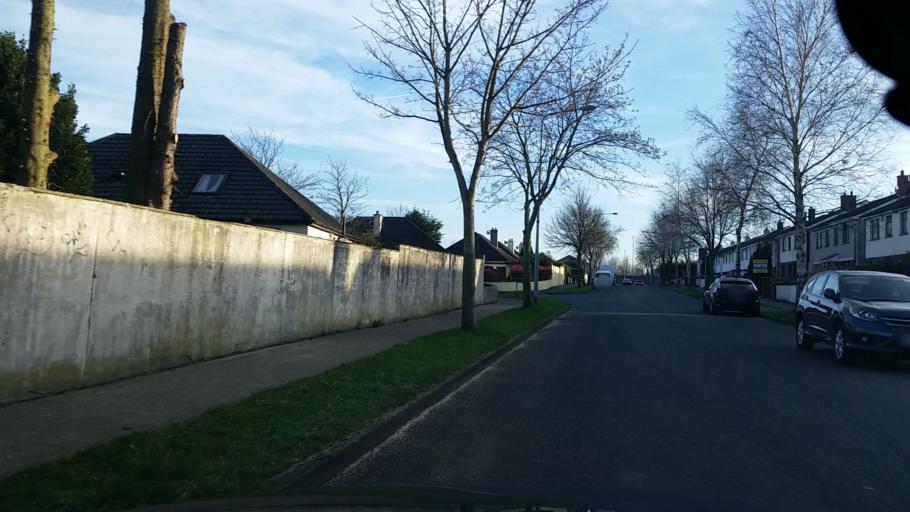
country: IE
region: Leinster
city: Hartstown
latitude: 53.3881
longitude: -6.4056
